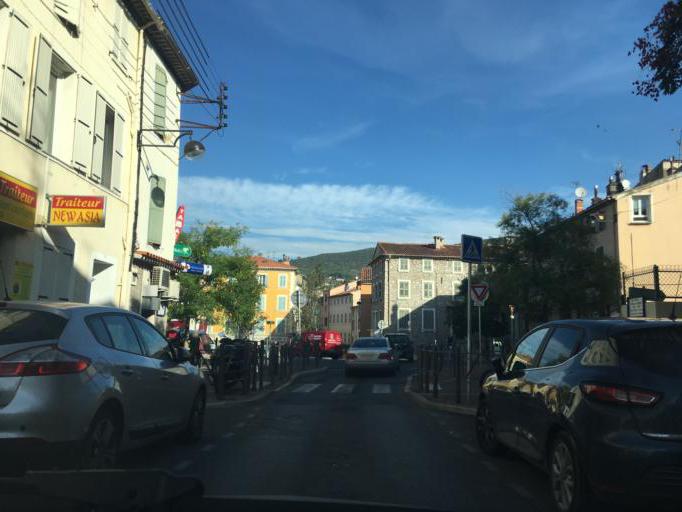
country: FR
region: Provence-Alpes-Cote d'Azur
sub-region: Departement du Var
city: Draguignan
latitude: 43.5364
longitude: 6.4684
